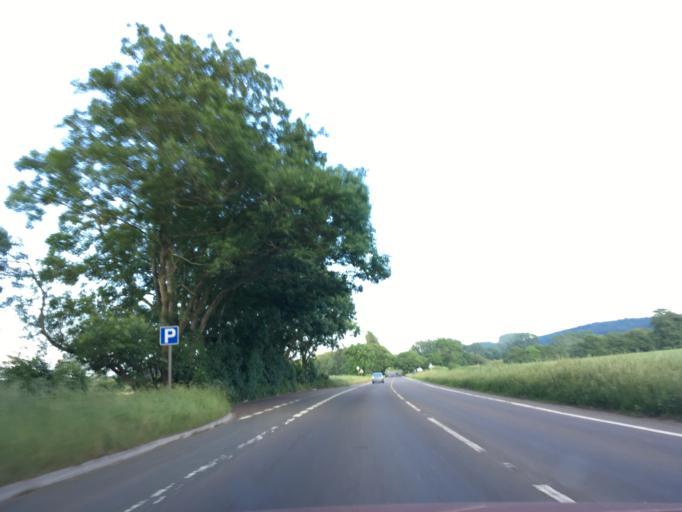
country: GB
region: England
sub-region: North Somerset
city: Churchill
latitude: 51.3397
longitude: -2.7780
